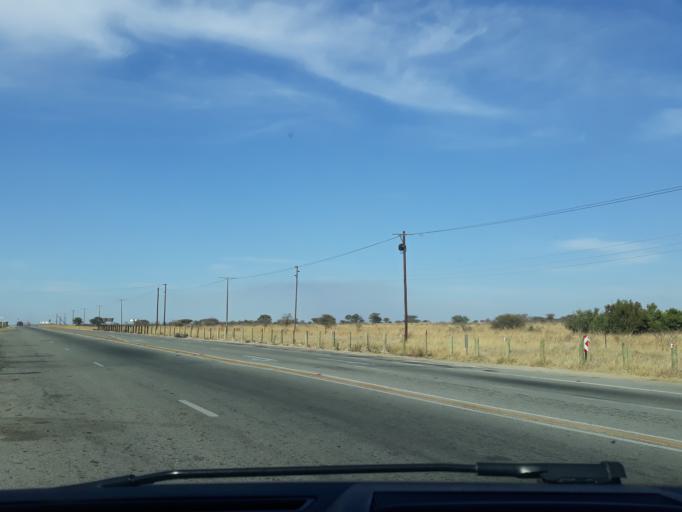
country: ZA
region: Limpopo
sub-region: Capricorn District Municipality
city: Polokwane
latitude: -23.9583
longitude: 29.3907
